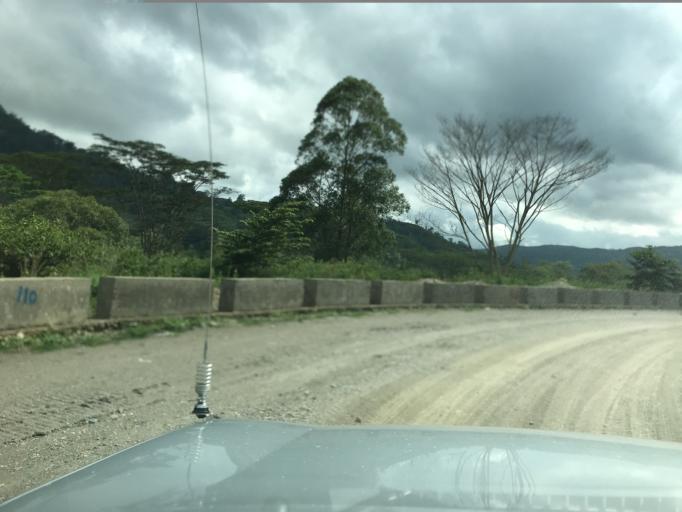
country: TL
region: Aileu
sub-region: Aileu Villa
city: Aileu
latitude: -8.6616
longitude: 125.5485
